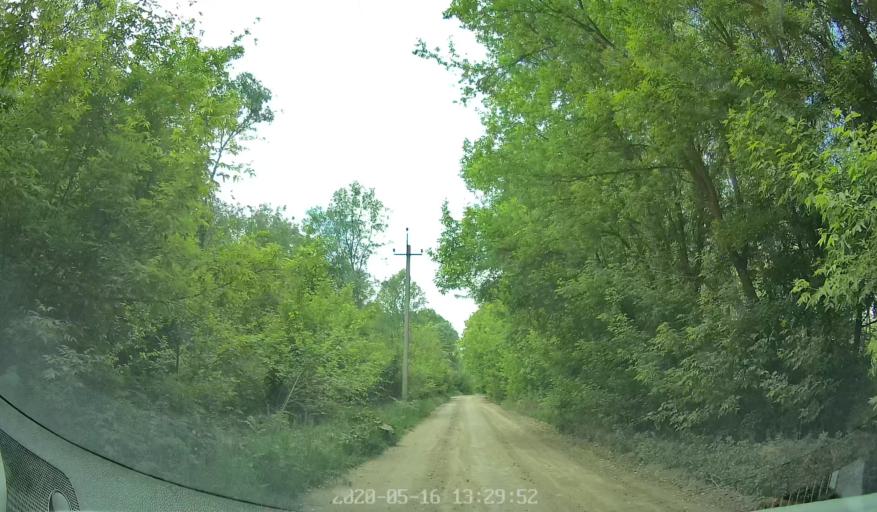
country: MD
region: Telenesti
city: Dnestrovsc
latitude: 46.5417
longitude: 29.9853
